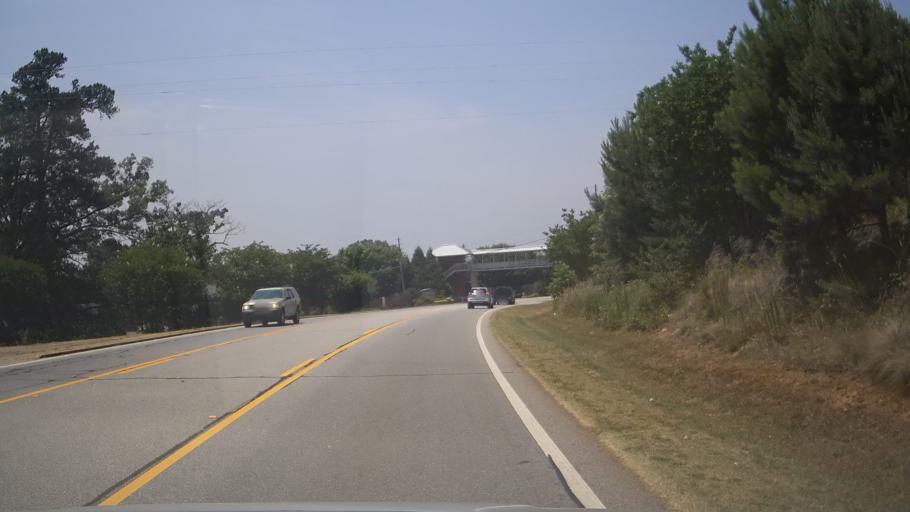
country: US
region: Georgia
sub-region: Hart County
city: Royston
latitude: 34.2843
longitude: -83.1464
